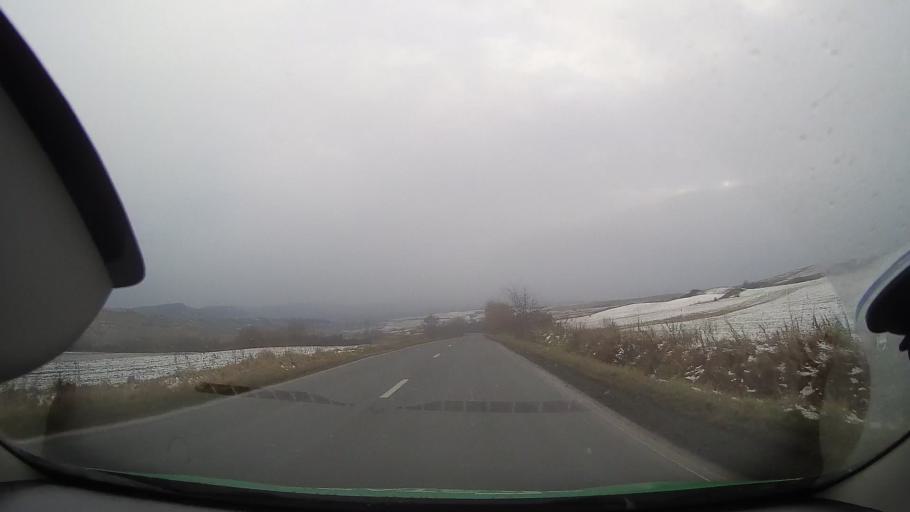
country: RO
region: Sibiu
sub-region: Comuna Blajel
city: Blajel
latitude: 46.2483
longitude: 24.3001
